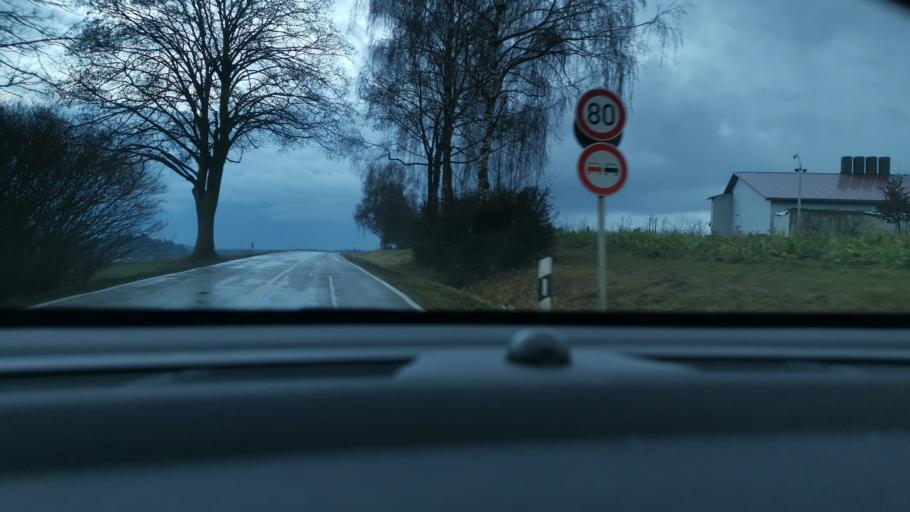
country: DE
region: Bavaria
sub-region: Swabia
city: Aindling
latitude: 48.5636
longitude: 10.9818
